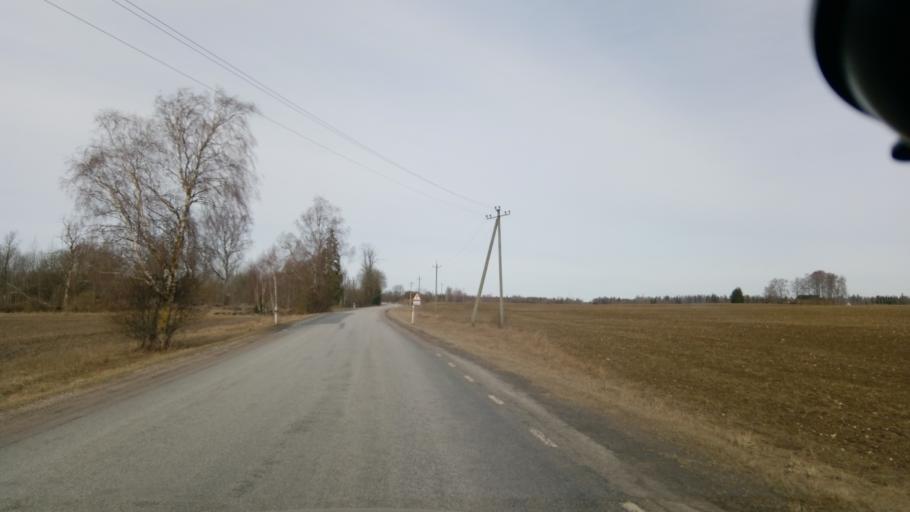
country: EE
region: Raplamaa
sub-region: Rapla vald
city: Rapla
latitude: 59.0285
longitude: 24.8378
